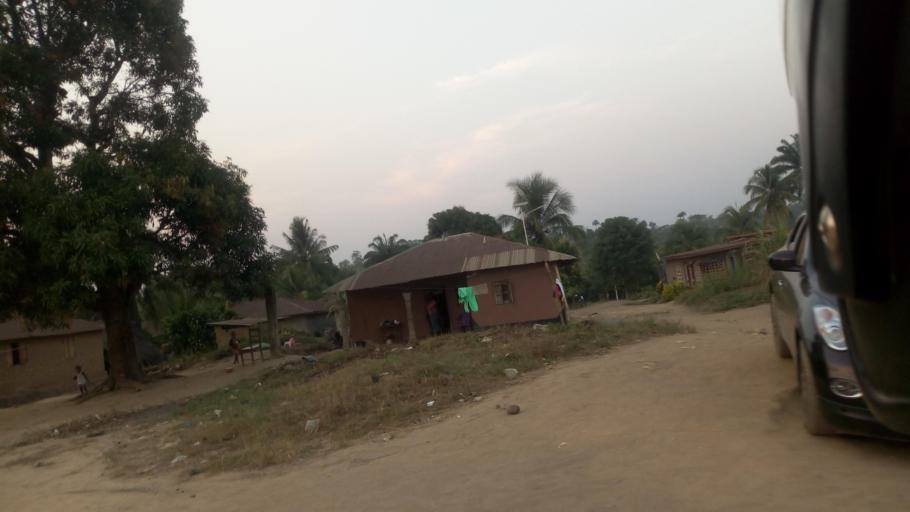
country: SL
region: Southern Province
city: Mogbwemo
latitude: 7.6073
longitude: -12.1713
